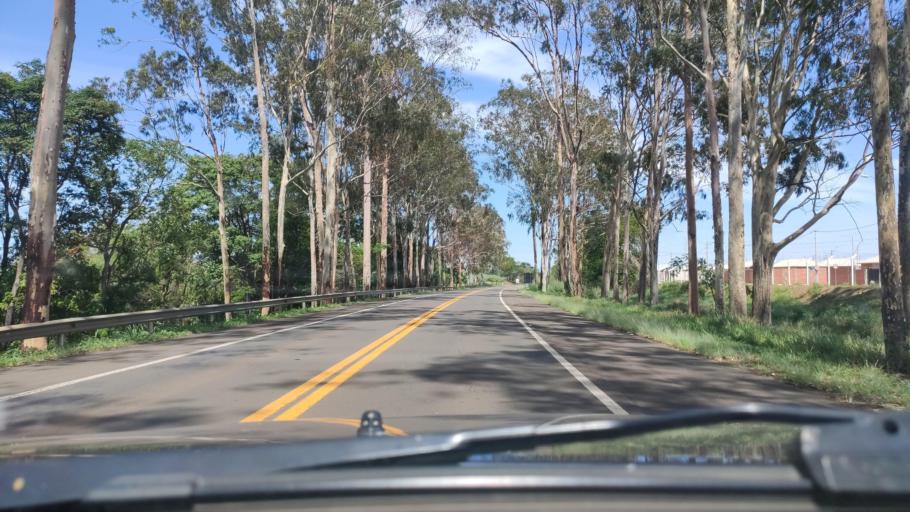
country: BR
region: Sao Paulo
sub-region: Sao Carlos
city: Sao Carlos
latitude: -22.0670
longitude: -47.9023
